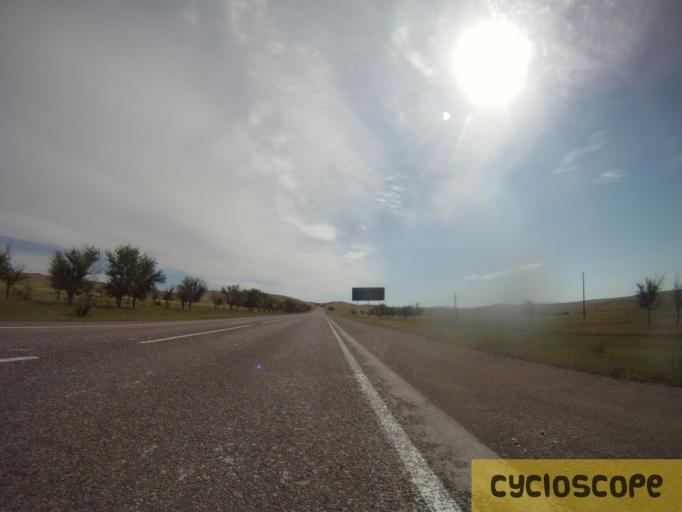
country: KZ
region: Zhambyl
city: Georgiyevka
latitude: 43.2522
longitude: 74.8065
